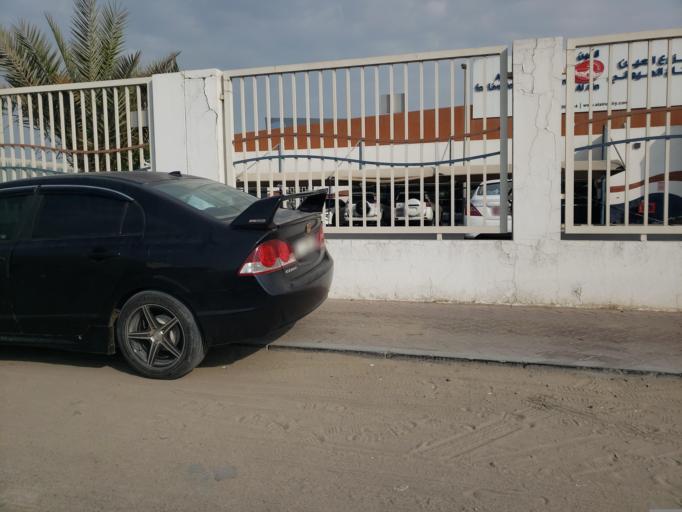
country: AE
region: Dubai
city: Dubai
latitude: 24.9846
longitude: 55.1132
